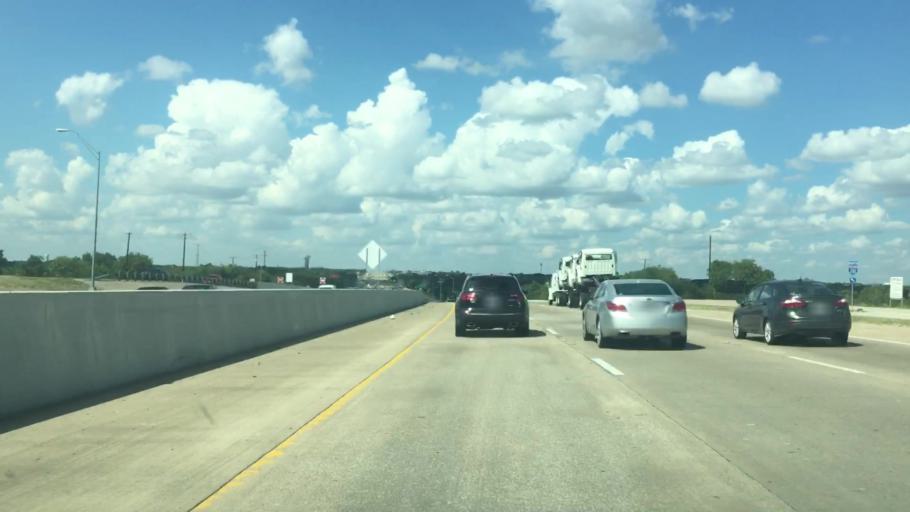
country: US
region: Texas
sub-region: Ellis County
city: Red Oak
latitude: 32.5000
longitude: -96.8222
